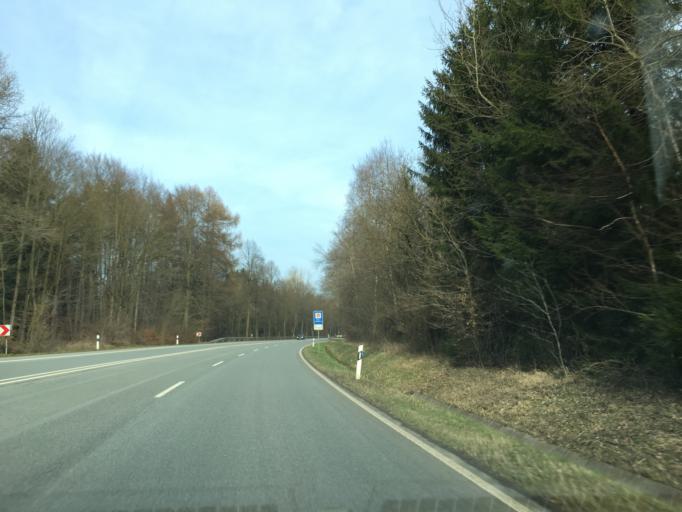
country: DE
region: North Rhine-Westphalia
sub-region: Regierungsbezirk Detmold
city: Willebadessen
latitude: 51.5645
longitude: 9.0029
